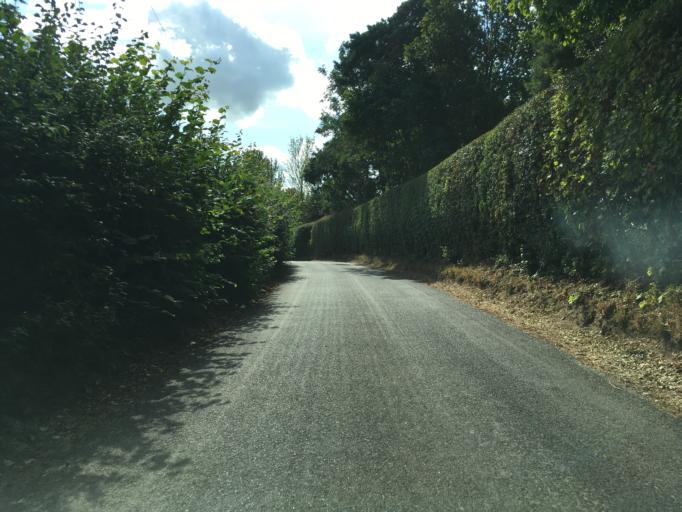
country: GB
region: England
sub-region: Kent
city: Maidstone
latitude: 51.2264
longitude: 0.5481
